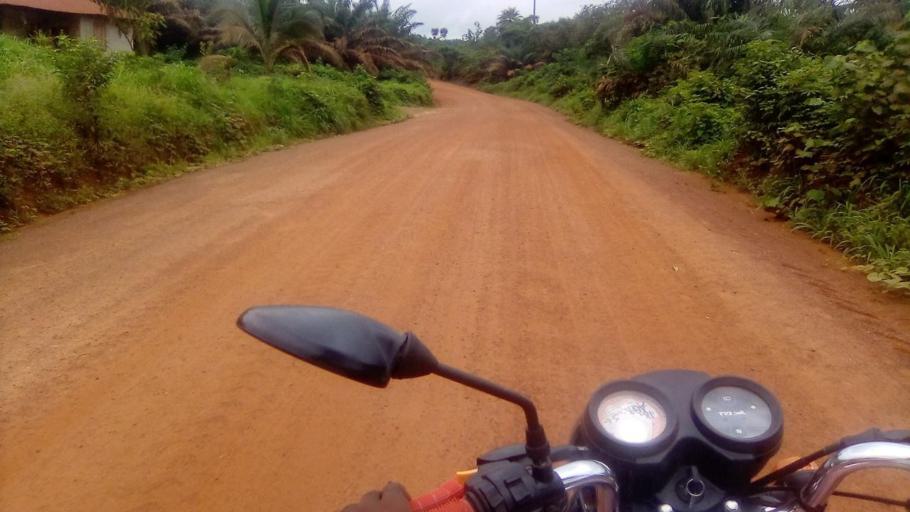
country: SL
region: Southern Province
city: Tongole
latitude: 7.4396
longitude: -11.8639
